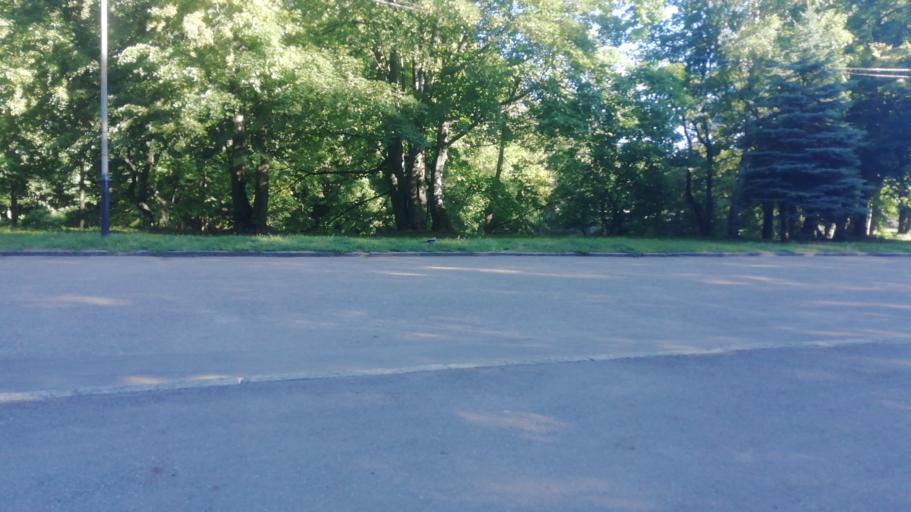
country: RU
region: Kaliningrad
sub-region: Gorod Kaliningrad
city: Kaliningrad
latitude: 54.6939
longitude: 20.5164
